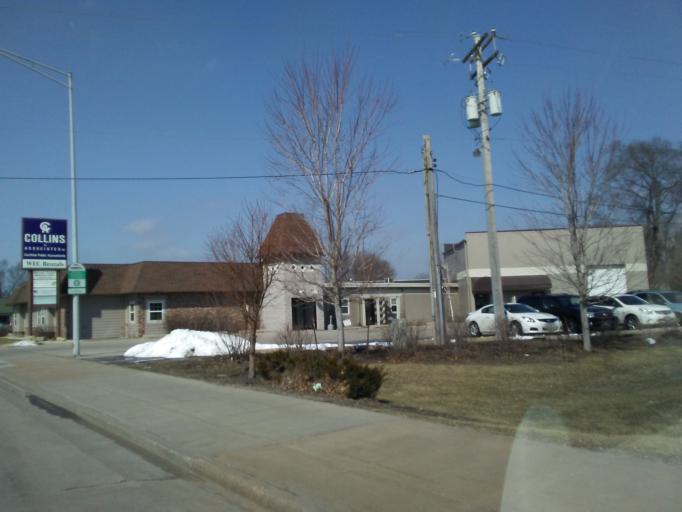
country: US
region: Wisconsin
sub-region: La Crosse County
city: La Crosse
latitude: 43.7765
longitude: -91.2211
